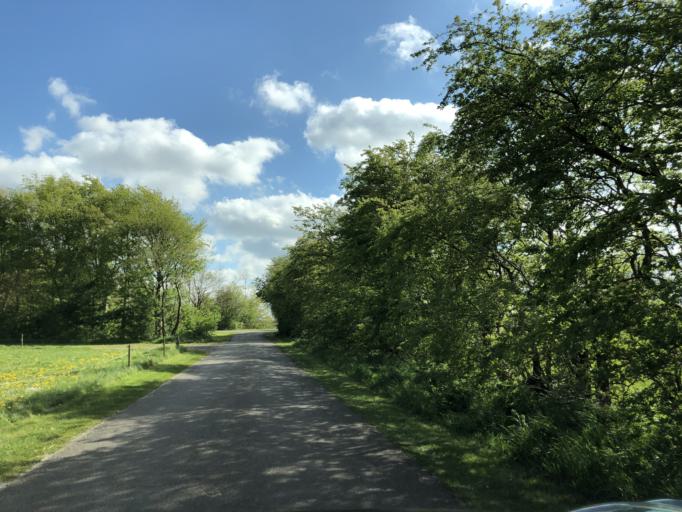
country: DK
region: Central Jutland
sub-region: Herning Kommune
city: Avlum
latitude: 56.2906
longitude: 8.7373
